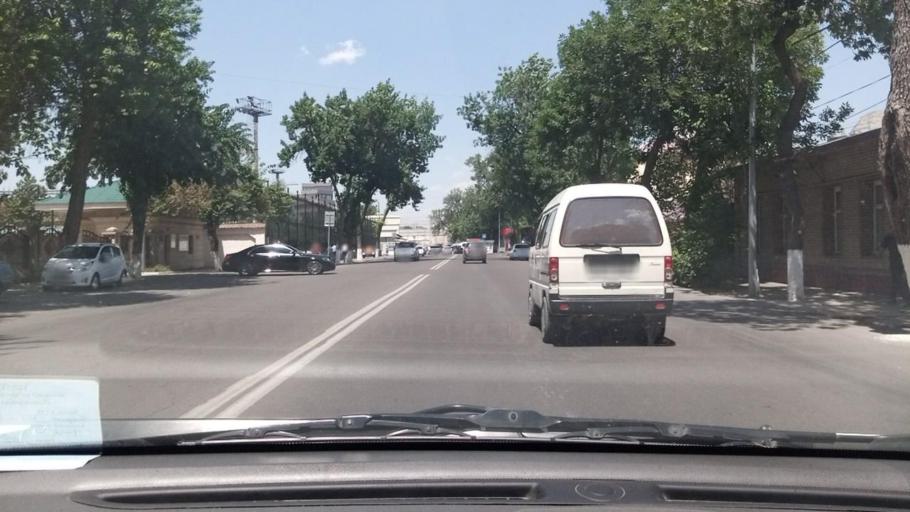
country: UZ
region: Toshkent Shahri
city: Tashkent
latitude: 41.2762
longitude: 69.2746
